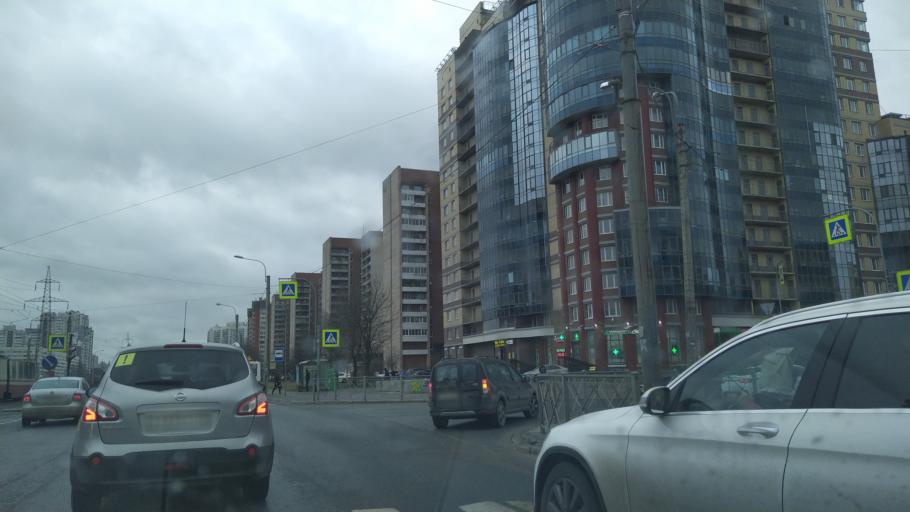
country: RU
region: St.-Petersburg
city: Komendantsky aerodrom
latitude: 60.0048
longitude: 30.2822
